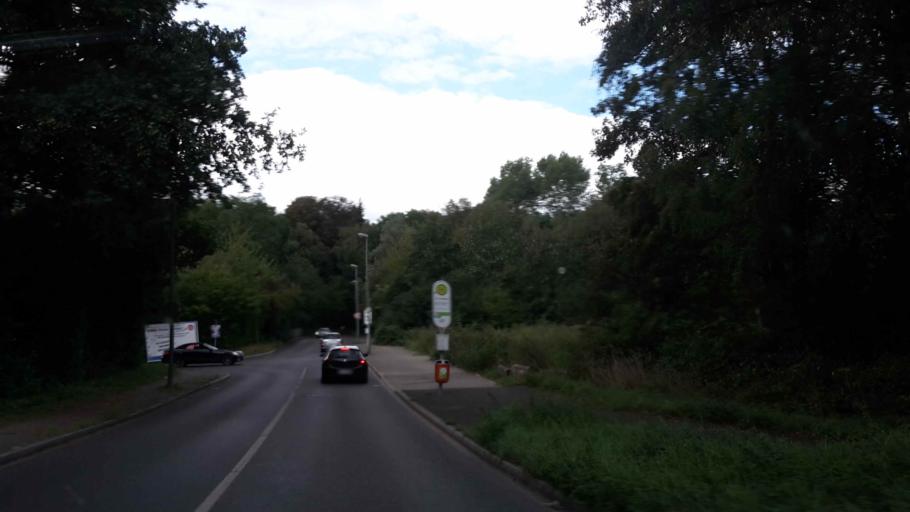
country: DE
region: North Rhine-Westphalia
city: Hattingen
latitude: 51.4326
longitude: 7.1635
